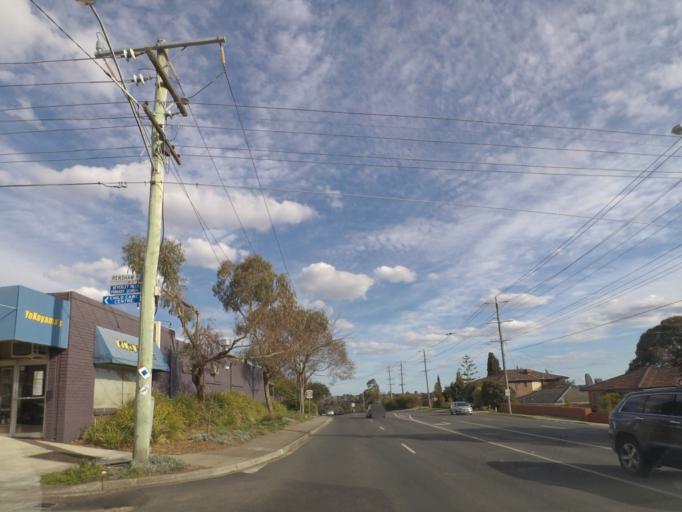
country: AU
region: Victoria
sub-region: Manningham
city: Doncaster East
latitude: -37.7939
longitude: 145.1425
